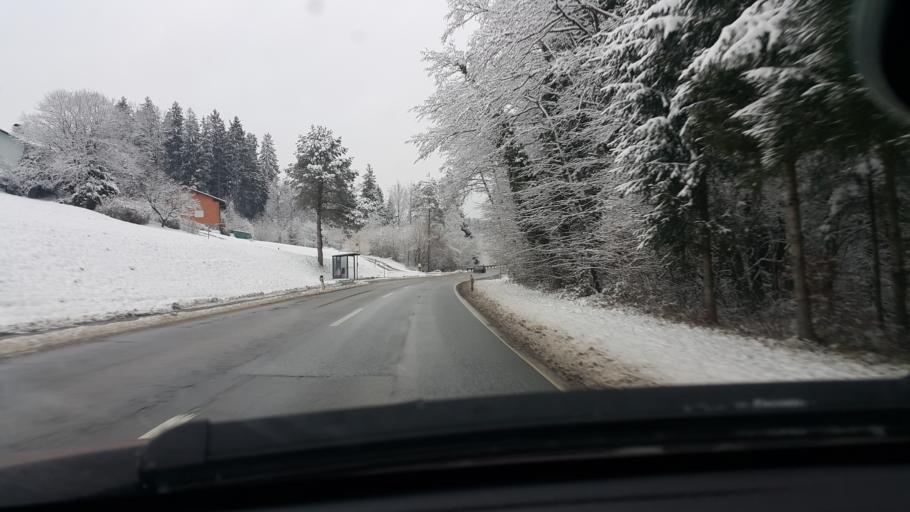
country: AT
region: Styria
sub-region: Politischer Bezirk Graz-Umgebung
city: Hitzendorf
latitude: 47.0204
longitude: 15.2873
